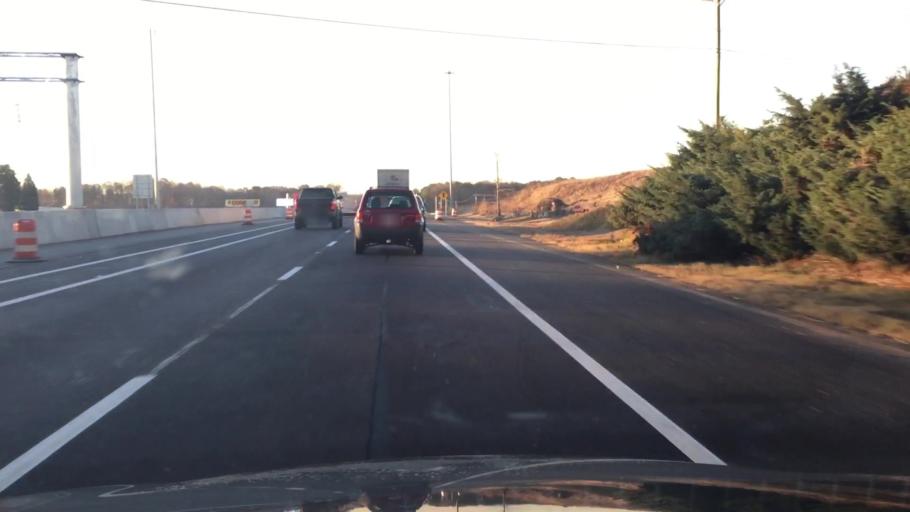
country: US
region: North Carolina
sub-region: Gaston County
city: Davidson
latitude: 35.5279
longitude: -80.8612
